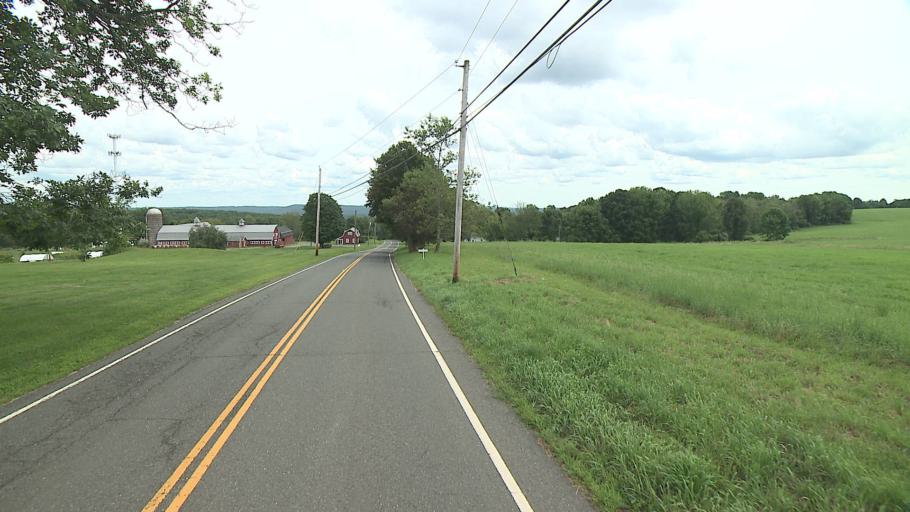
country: US
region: Connecticut
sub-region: Litchfield County
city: Woodbury
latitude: 41.5569
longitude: -73.2594
